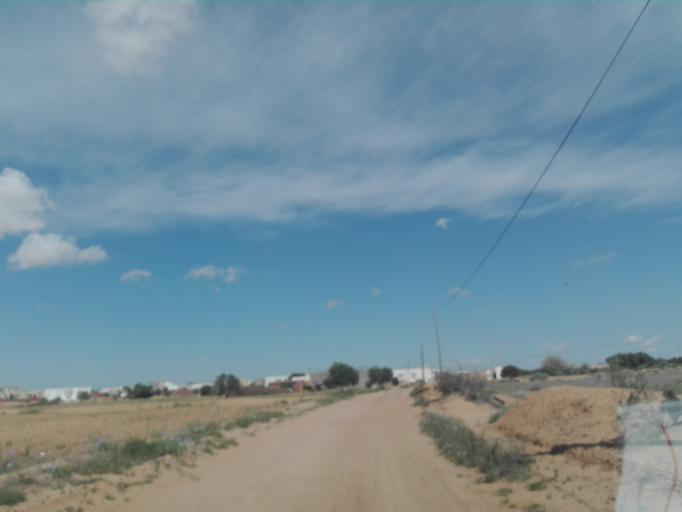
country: TN
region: Safaqis
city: Sfax
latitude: 34.7309
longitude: 10.5089
